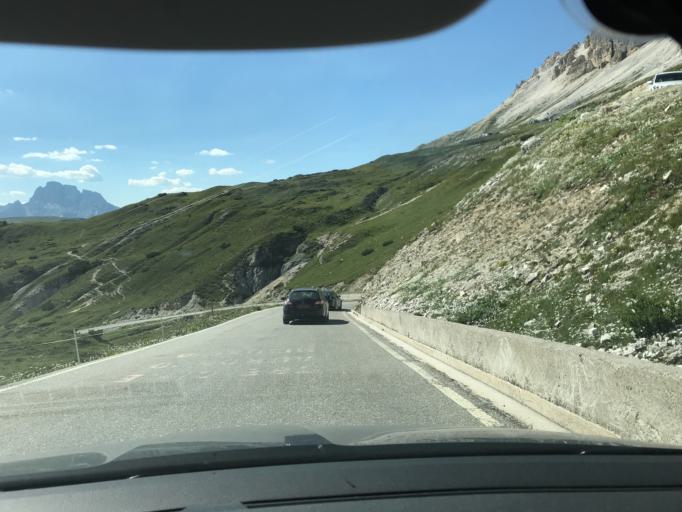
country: IT
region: Trentino-Alto Adige
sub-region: Bolzano
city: Sesto
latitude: 46.6085
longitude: 12.2972
